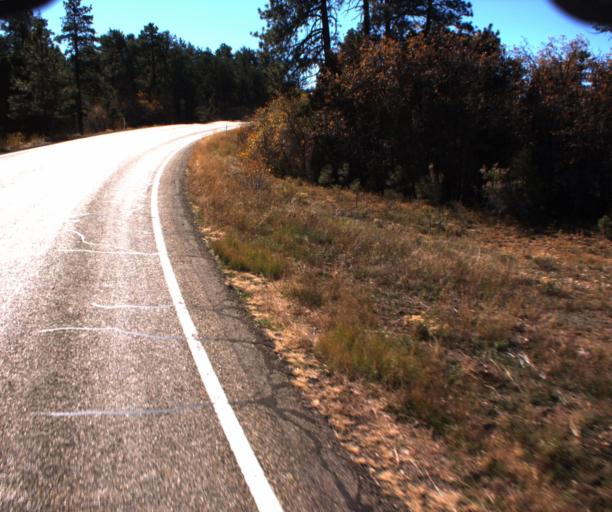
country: US
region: Arizona
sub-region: Coconino County
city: Fredonia
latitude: 36.7884
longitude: -112.2575
